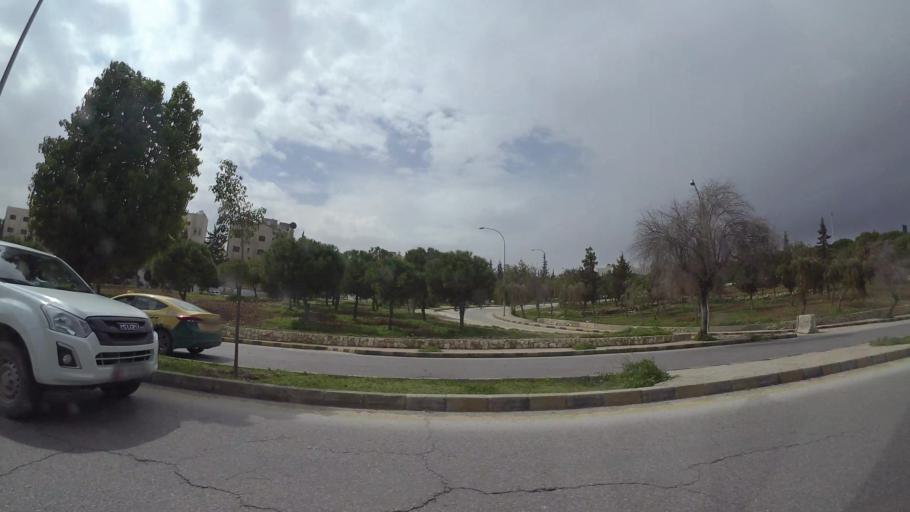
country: JO
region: Amman
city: Amman
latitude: 31.9790
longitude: 35.9183
